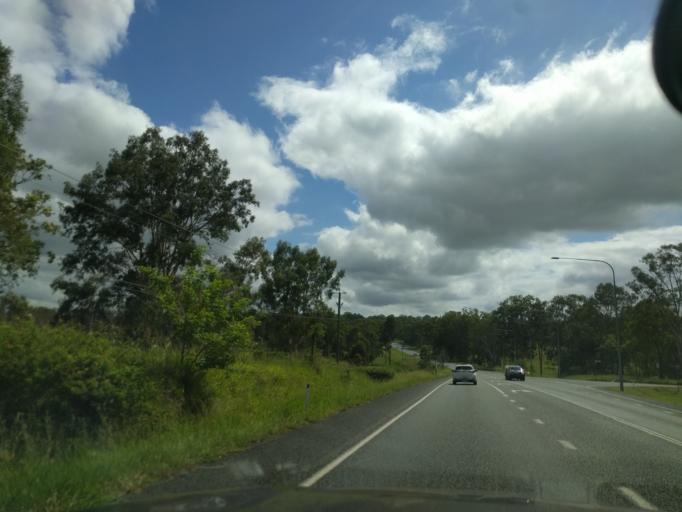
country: AU
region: Queensland
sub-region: Logan
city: Cedar Vale
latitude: -27.8856
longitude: 152.9805
